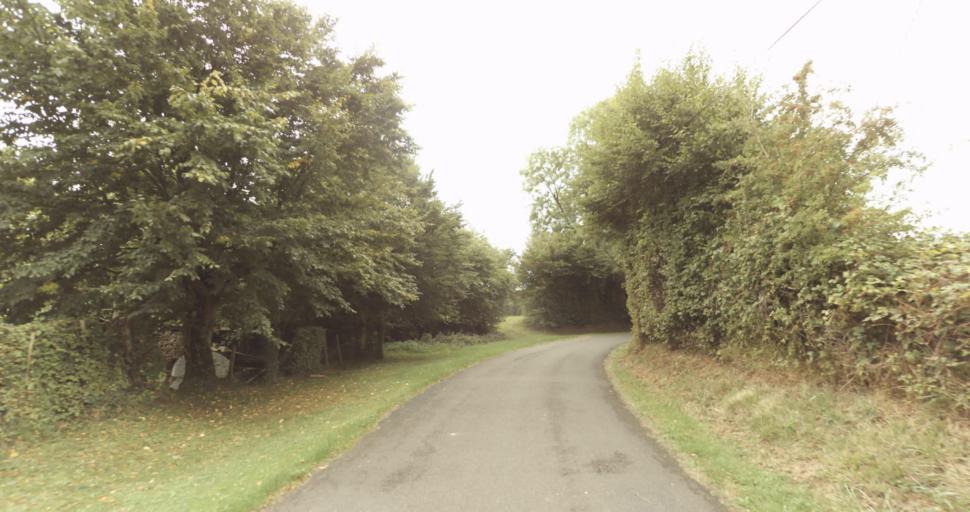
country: FR
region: Lower Normandy
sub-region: Departement de l'Orne
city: Gace
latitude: 48.6738
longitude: 0.3136
